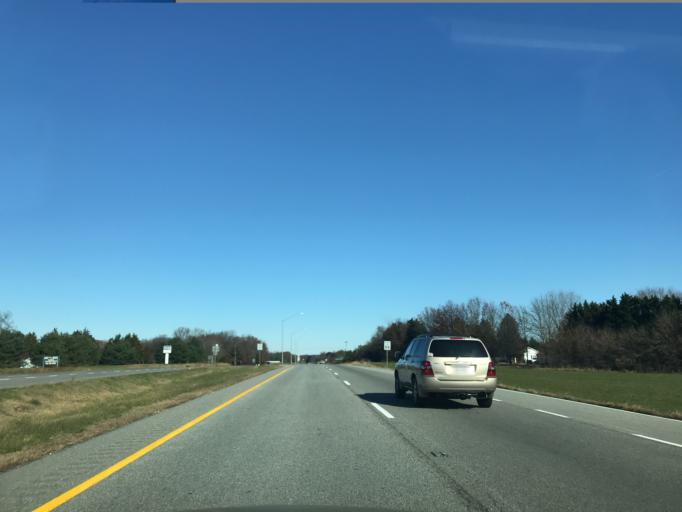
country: US
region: Maryland
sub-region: Queen Anne's County
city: Kingstown
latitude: 39.2421
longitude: -75.8737
